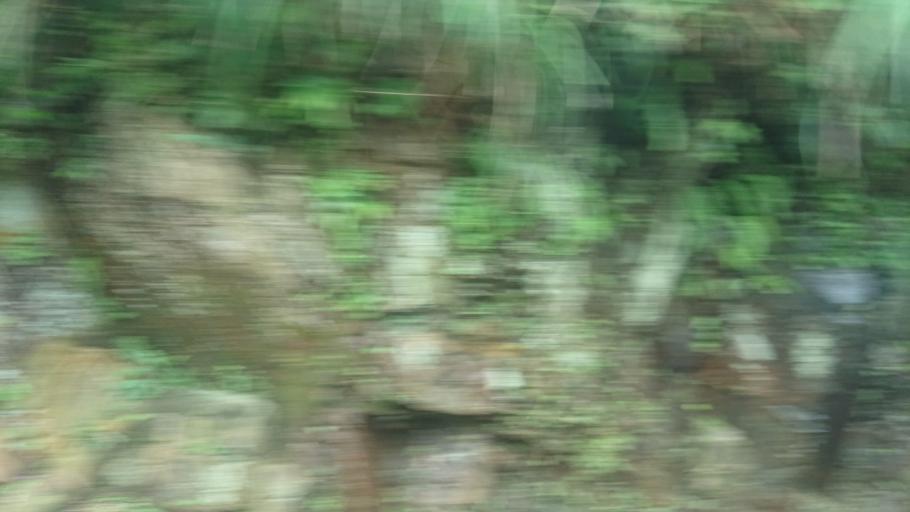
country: TW
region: Taiwan
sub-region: Keelung
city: Keelung
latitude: 25.1082
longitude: 121.8417
